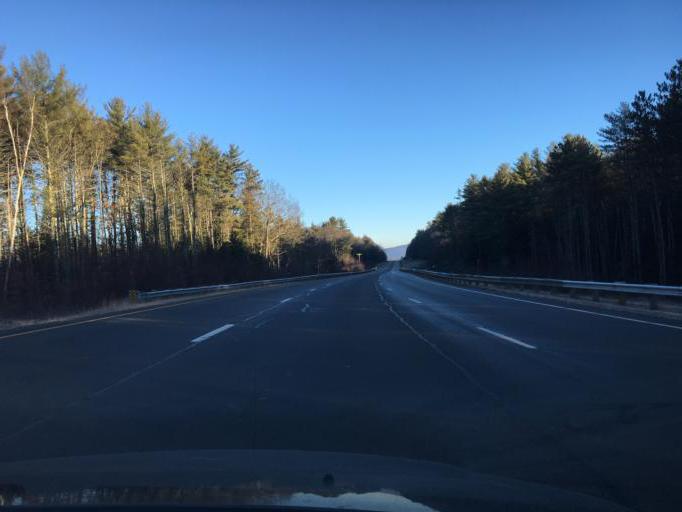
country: US
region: New Hampshire
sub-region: Belknap County
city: Sanbornton
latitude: 43.5090
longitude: -71.6171
